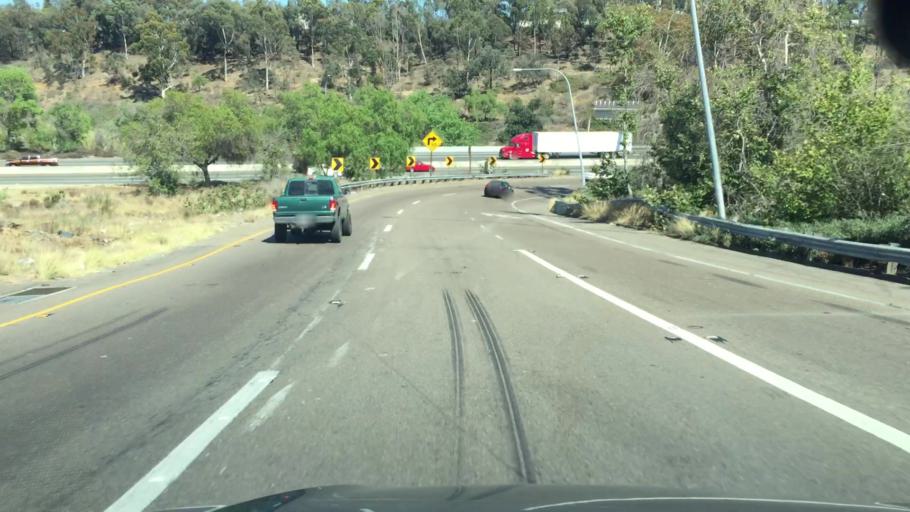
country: US
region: California
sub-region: San Diego County
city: San Diego
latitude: 32.7153
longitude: -117.1191
